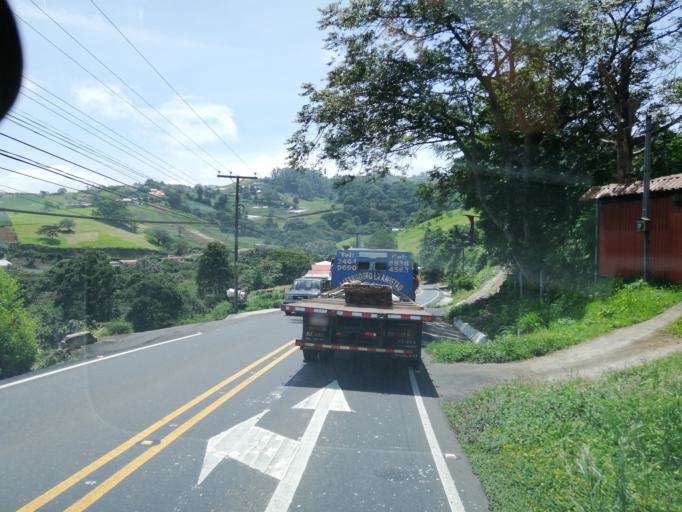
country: CR
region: Alajuela
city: Zarcero
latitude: 10.2135
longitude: -84.4009
